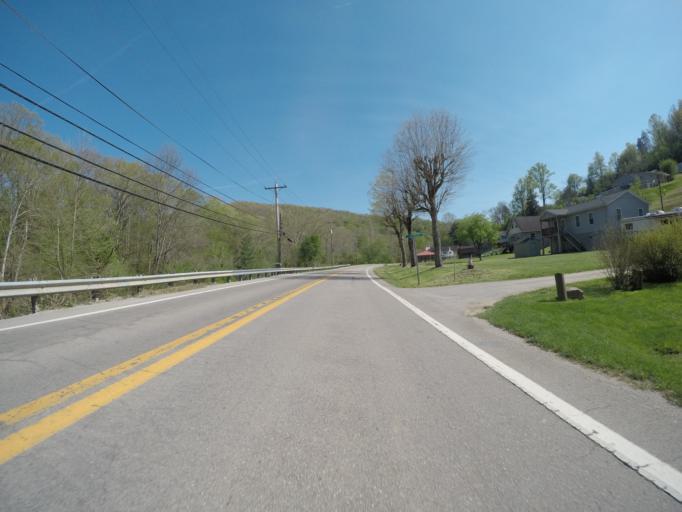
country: US
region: West Virginia
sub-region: Kanawha County
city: Clendenin
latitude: 38.5021
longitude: -81.3490
